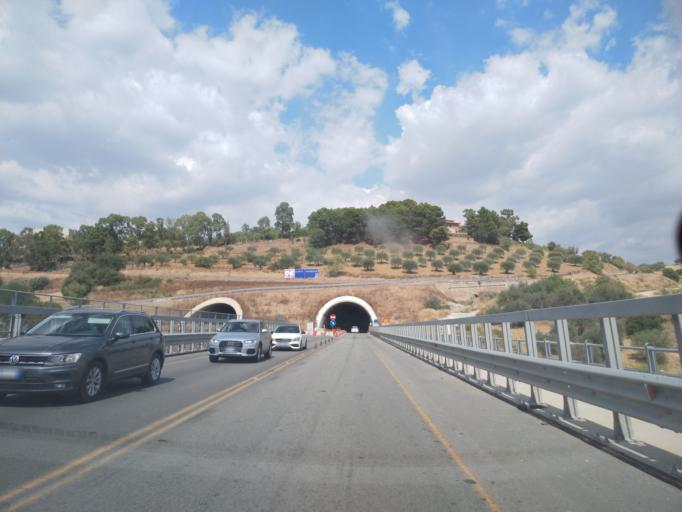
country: IT
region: Sicily
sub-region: Provincia di Caltanissetta
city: San Cataldo
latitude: 37.4587
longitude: 13.9947
